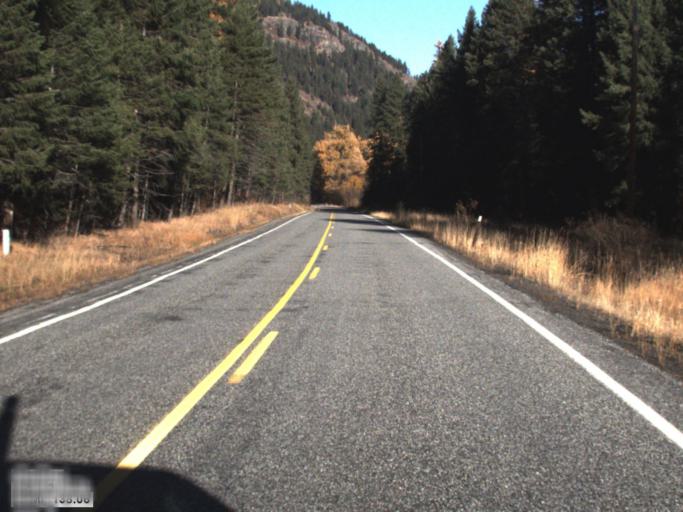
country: US
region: Washington
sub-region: Ferry County
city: Republic
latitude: 48.3630
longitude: -118.7421
